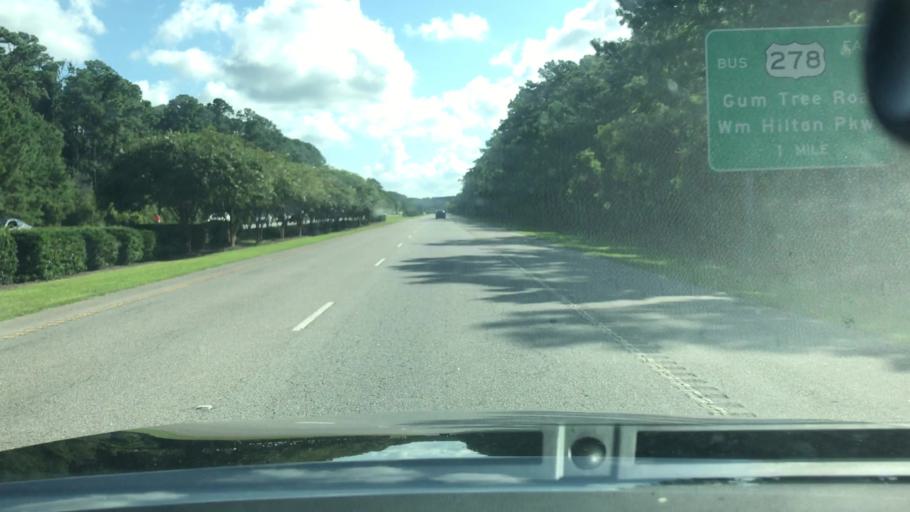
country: US
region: South Carolina
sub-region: Beaufort County
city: Hilton Head Island
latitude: 32.2014
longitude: -80.7521
